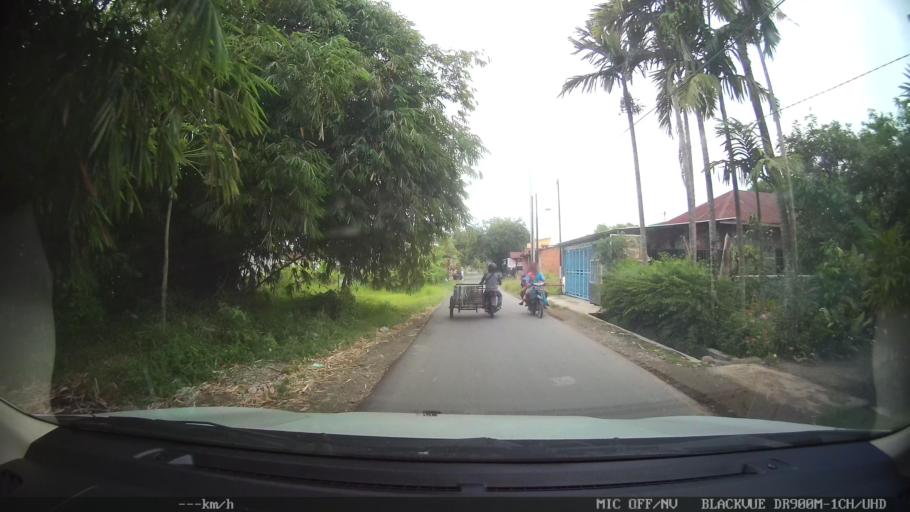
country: ID
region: North Sumatra
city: Sunggal
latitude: 3.6208
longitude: 98.5914
